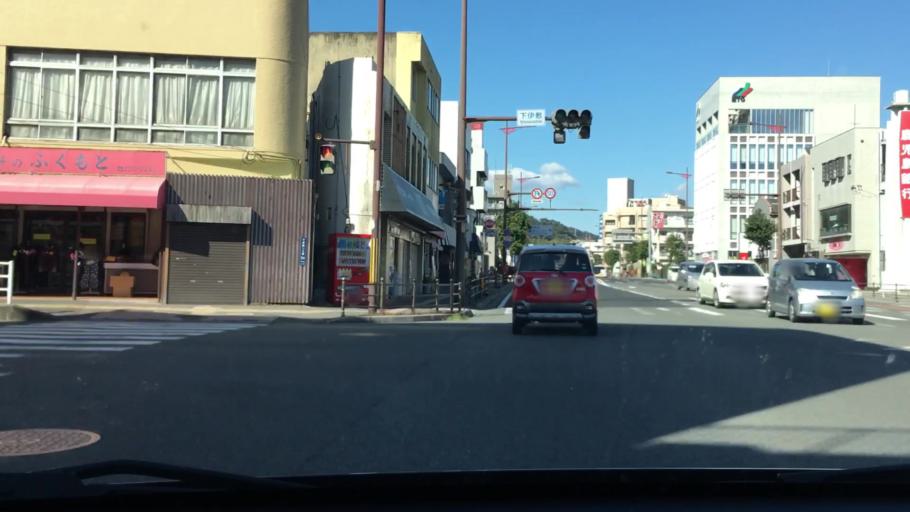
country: JP
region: Kagoshima
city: Kagoshima-shi
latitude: 31.6146
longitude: 130.5302
